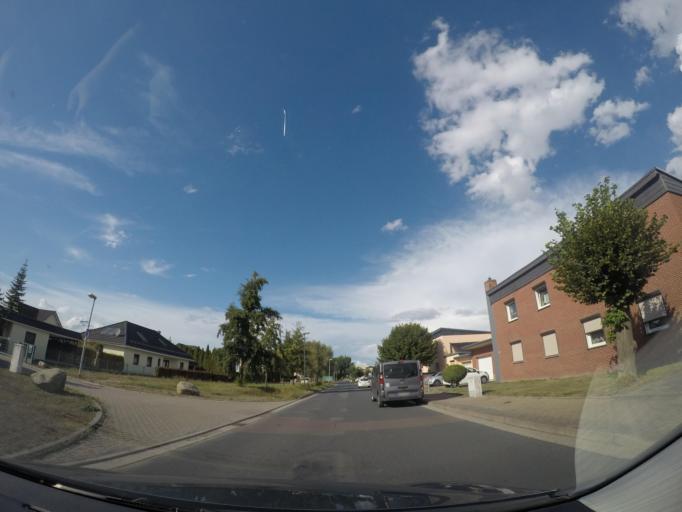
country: DE
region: Saxony-Anhalt
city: Diesdorf
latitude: 52.1391
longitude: 11.5801
